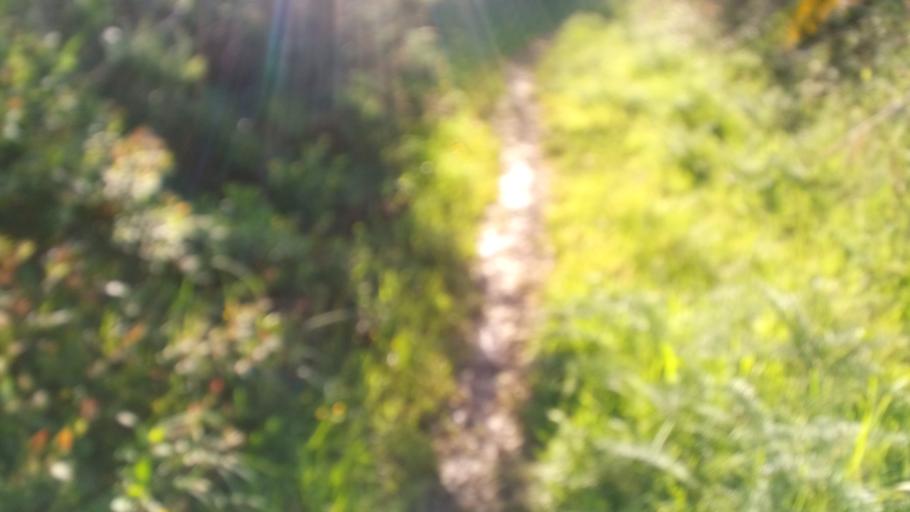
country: PT
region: Leiria
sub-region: Caldas da Rainha
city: Caldas da Rainha
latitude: 39.4528
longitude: -9.1974
